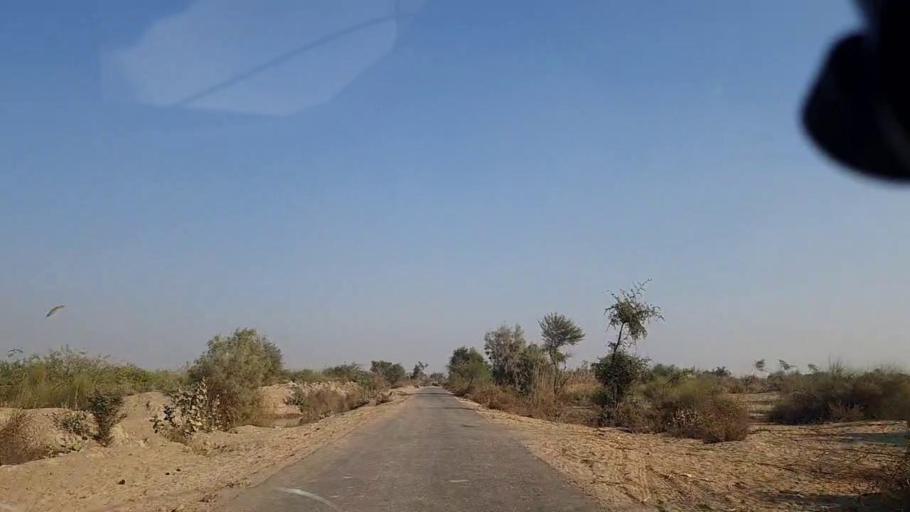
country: PK
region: Sindh
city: Khanpur
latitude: 27.6856
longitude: 69.5244
